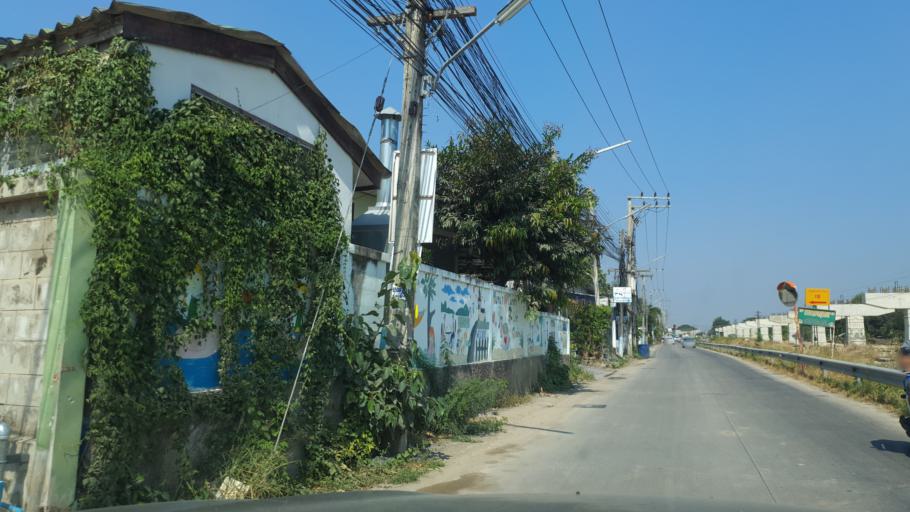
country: TH
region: Prachuap Khiri Khan
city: Hua Hin
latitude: 12.5575
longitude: 99.9568
